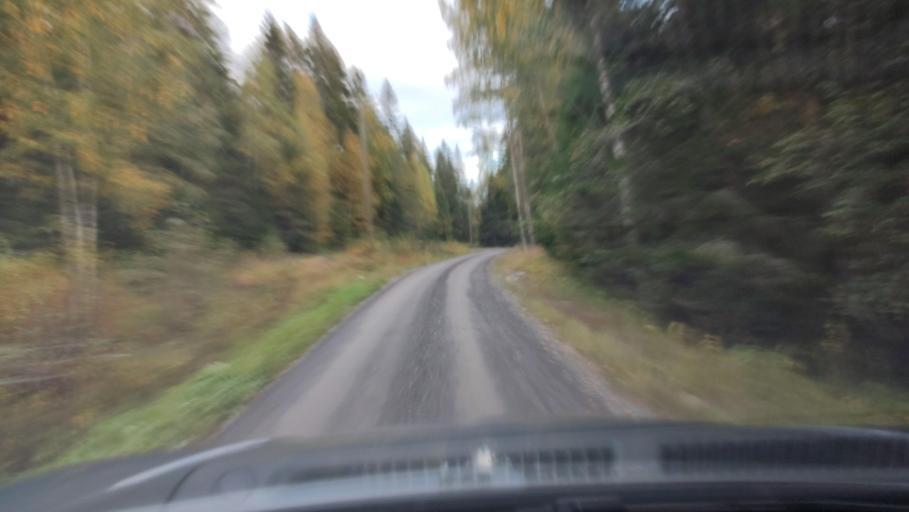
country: FI
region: Ostrobothnia
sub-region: Sydosterbotten
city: Kristinestad
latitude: 62.2358
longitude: 21.3944
